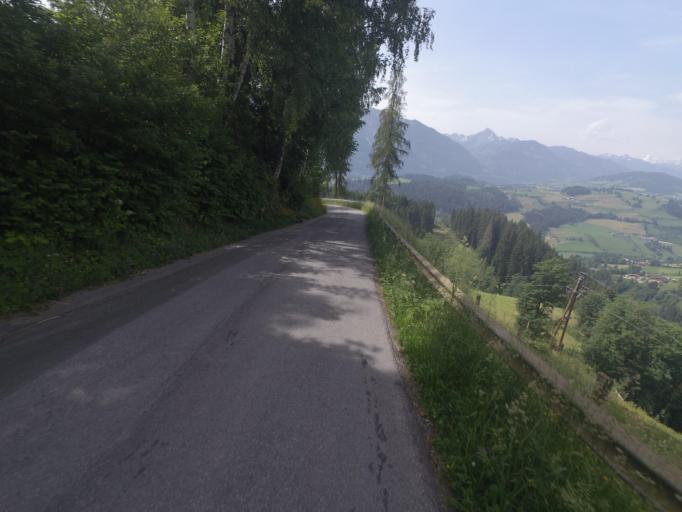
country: AT
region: Salzburg
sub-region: Politischer Bezirk Sankt Johann im Pongau
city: Sankt Veit im Pongau
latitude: 47.3408
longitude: 13.1301
